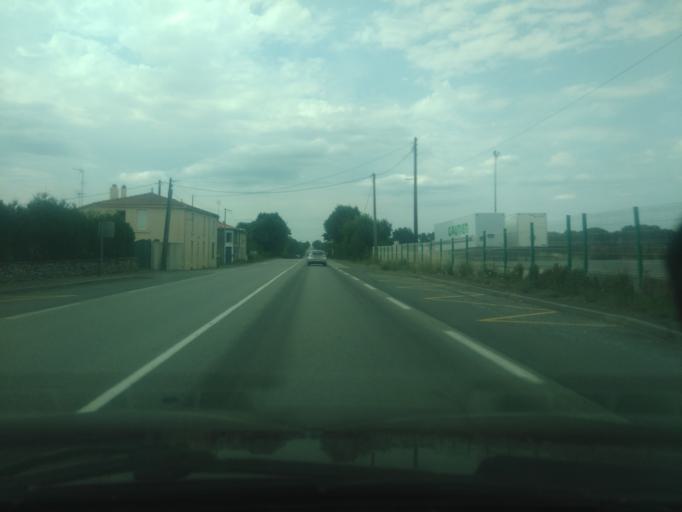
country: FR
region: Pays de la Loire
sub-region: Departement de la Vendee
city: Chantonnay
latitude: 46.7065
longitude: -1.0633
